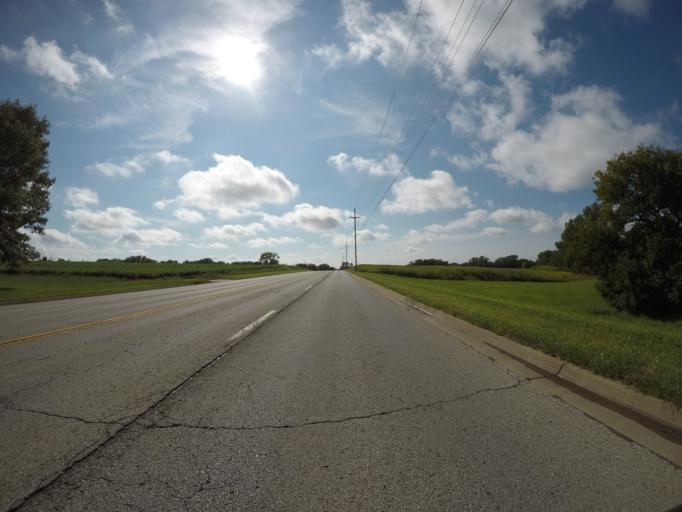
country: US
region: Kansas
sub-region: Leavenworth County
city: Basehor
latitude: 39.1287
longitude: -94.8772
